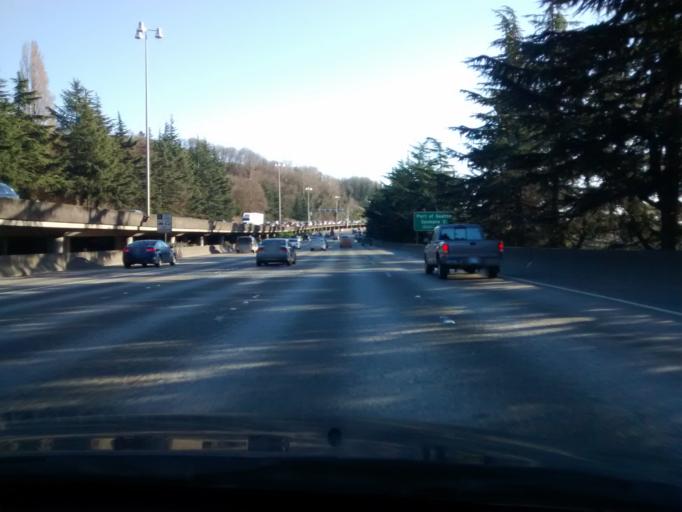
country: US
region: Washington
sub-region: King County
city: Seattle
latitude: 47.5827
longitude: -122.3200
